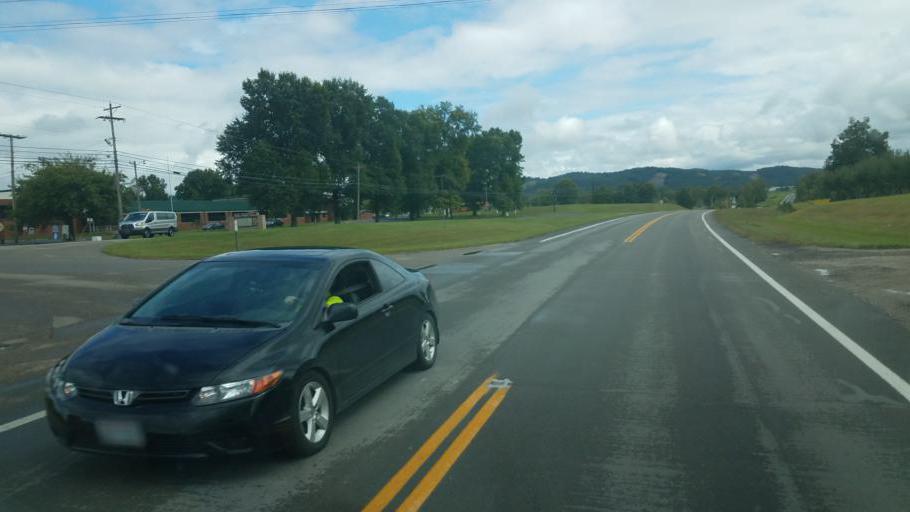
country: US
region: Ohio
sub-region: Scioto County
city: Lucasville
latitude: 38.8800
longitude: -82.9781
